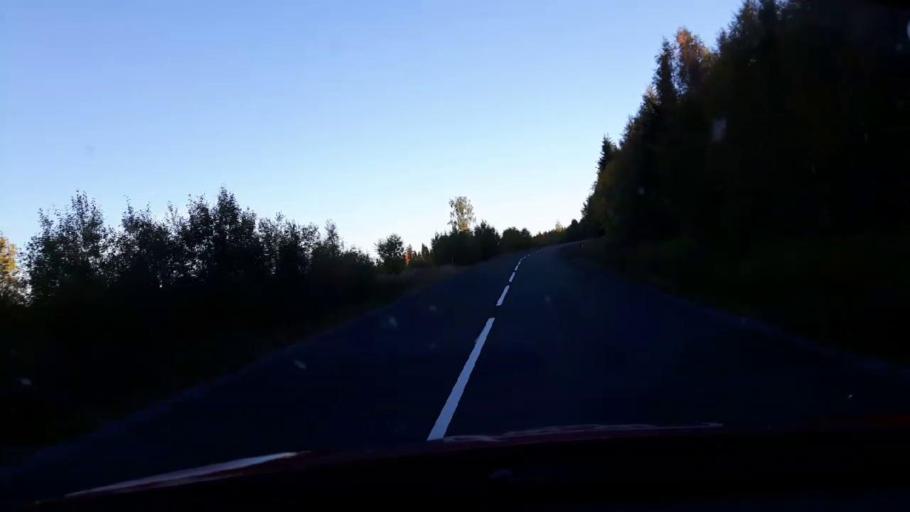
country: SE
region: Jaemtland
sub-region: OEstersunds Kommun
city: Lit
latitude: 63.4794
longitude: 14.8803
